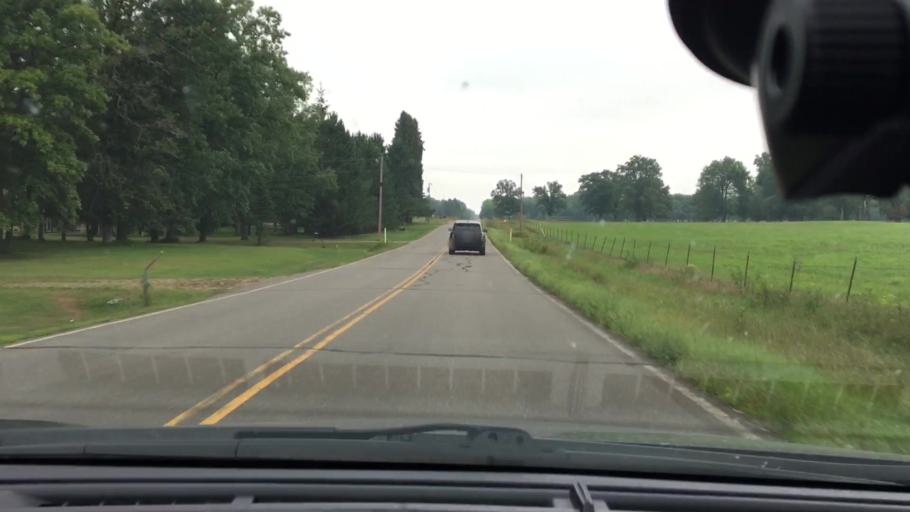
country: US
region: Minnesota
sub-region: Crow Wing County
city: Cross Lake
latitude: 46.6425
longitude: -94.0097
